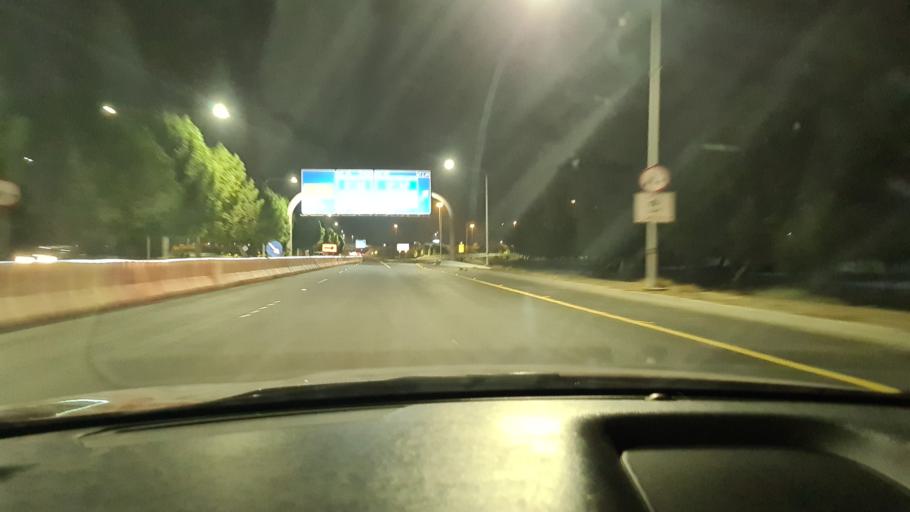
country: SA
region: Eastern Province
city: Al Jubayl
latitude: 27.1333
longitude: 49.5537
